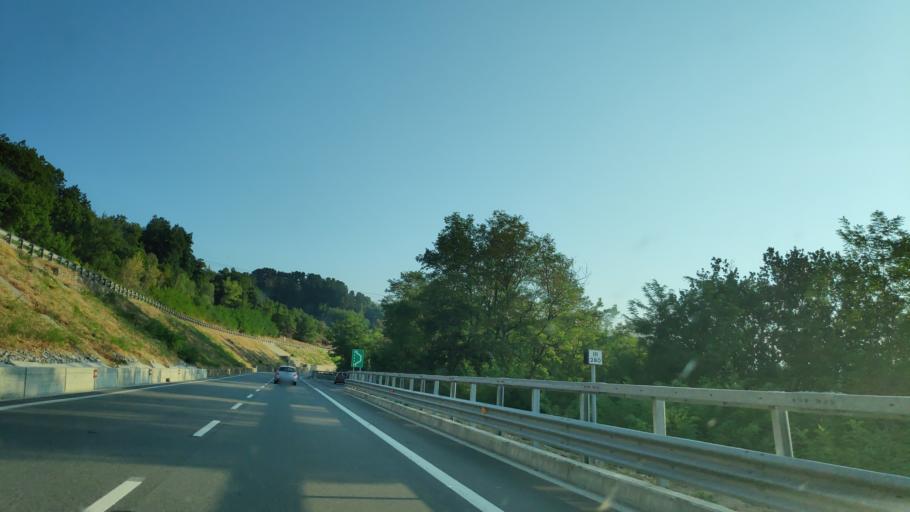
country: IT
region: Calabria
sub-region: Provincia di Cosenza
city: Belsito
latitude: 39.1603
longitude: 16.2869
